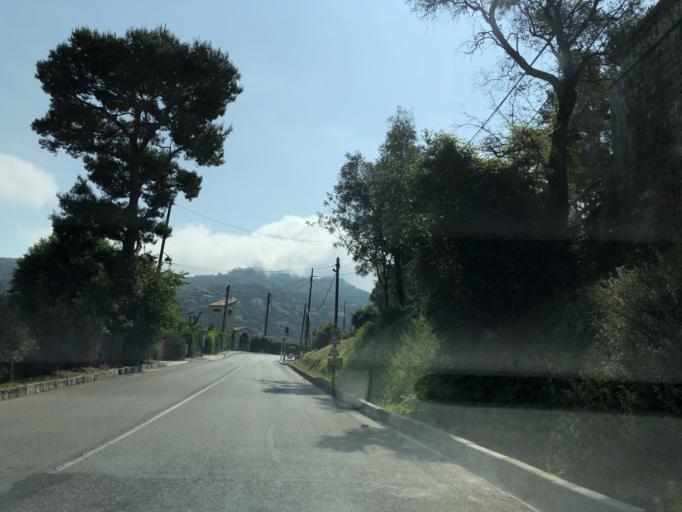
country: FR
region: Provence-Alpes-Cote d'Azur
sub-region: Departement des Alpes-Maritimes
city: Villefranche-sur-Mer
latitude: 43.7209
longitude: 7.3034
